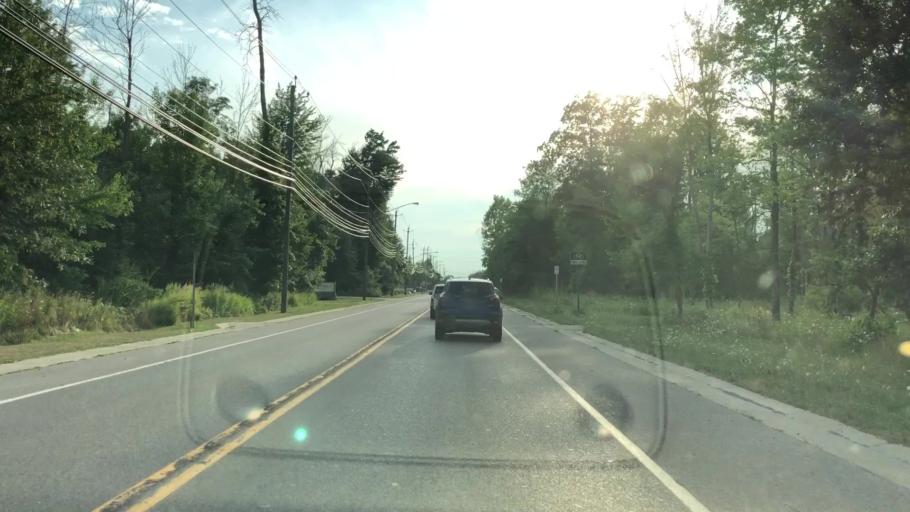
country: US
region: New York
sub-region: Erie County
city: Cheektowaga
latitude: 42.8931
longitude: -78.7473
